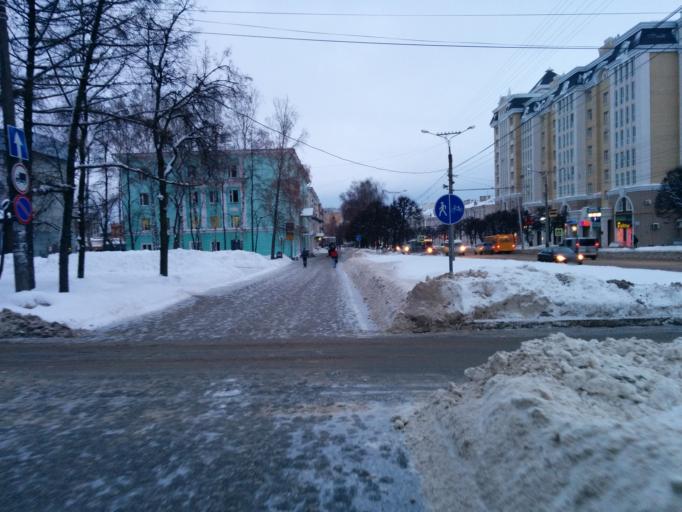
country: RU
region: Chuvashia
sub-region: Cheboksarskiy Rayon
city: Cheboksary
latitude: 56.1290
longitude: 47.2482
